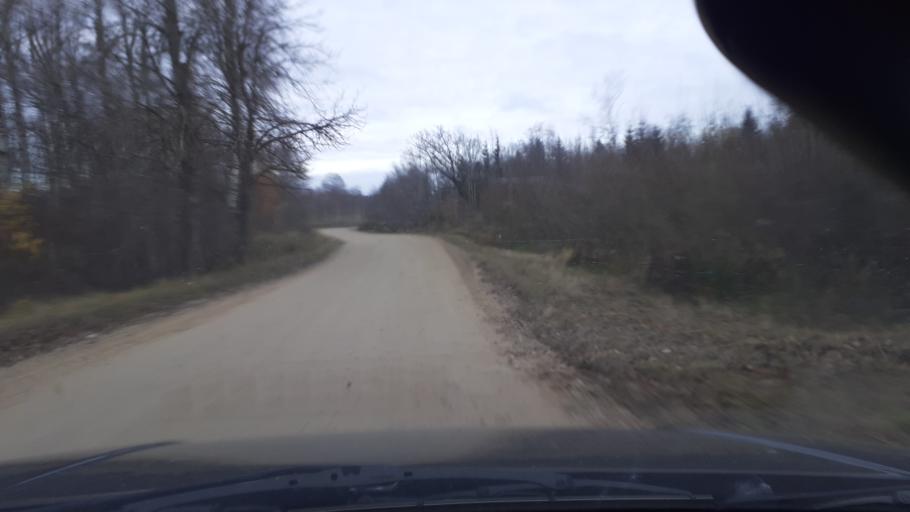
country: LV
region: Alsunga
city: Alsunga
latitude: 56.9502
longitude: 21.6436
